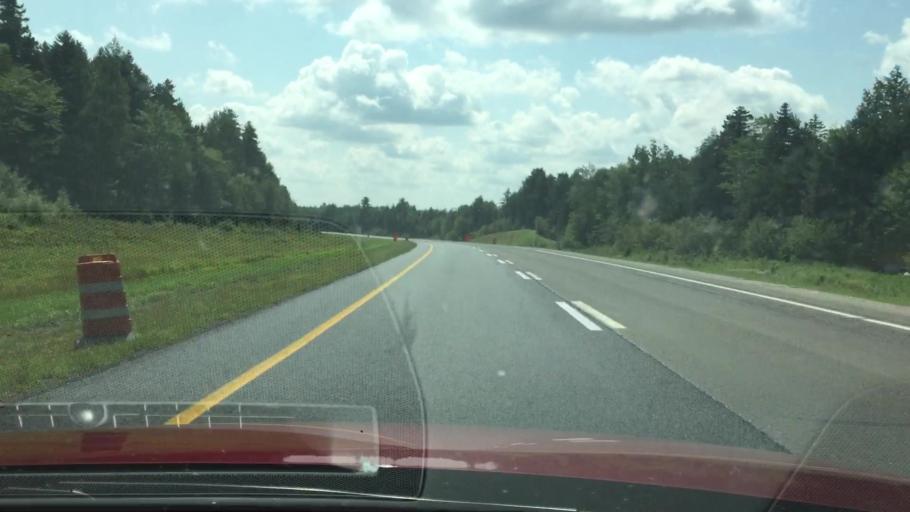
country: US
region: Maine
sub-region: Penobscot County
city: Medway
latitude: 45.7010
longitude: -68.4851
